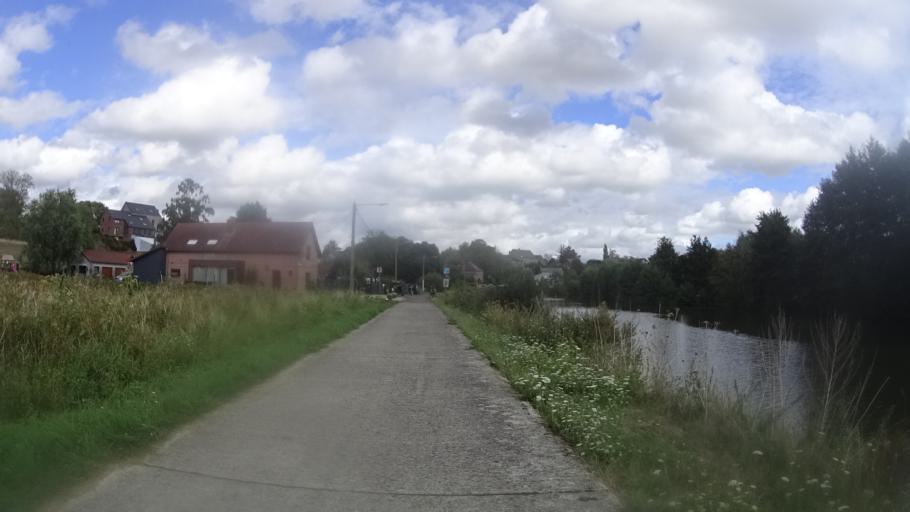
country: BE
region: Wallonia
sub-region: Province du Hainaut
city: Merbes-le-Chateau
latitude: 50.3191
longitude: 4.1764
